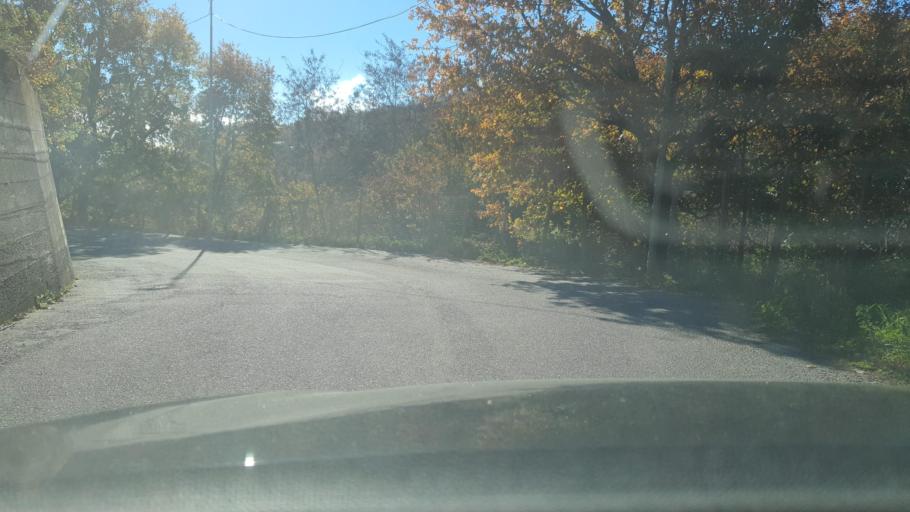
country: IT
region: Calabria
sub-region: Provincia di Catanzaro
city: Sant'Elia
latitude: 38.9638
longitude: 16.5788
